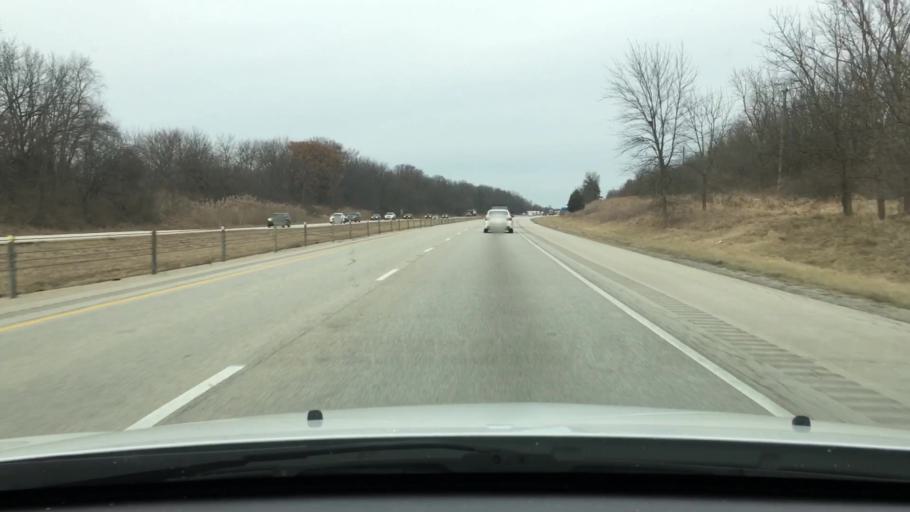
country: US
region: Illinois
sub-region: Sangamon County
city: Sherman
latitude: 39.8764
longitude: -89.5965
